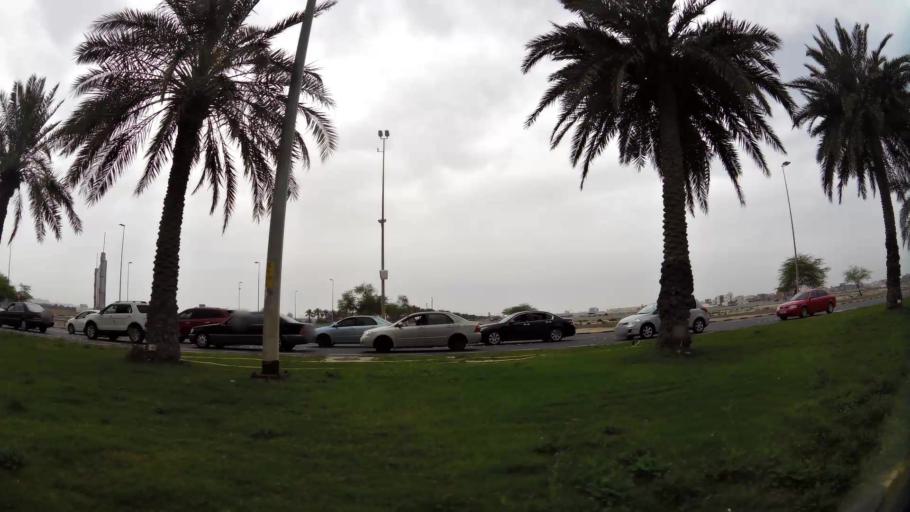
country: BH
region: Central Governorate
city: Dar Kulayb
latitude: 26.0567
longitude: 50.4988
